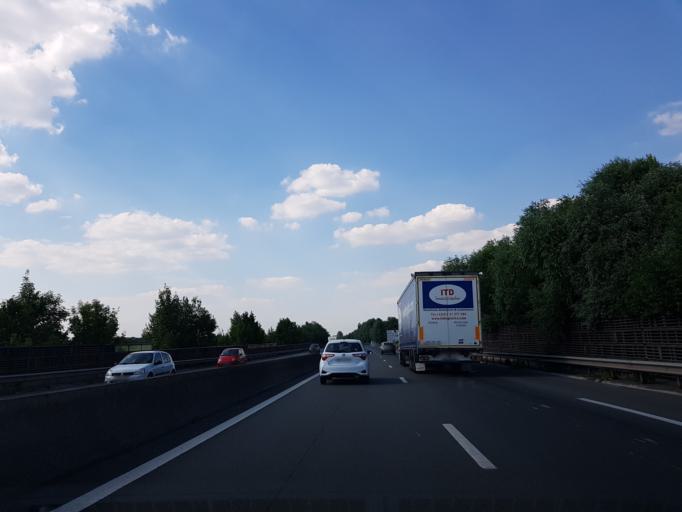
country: FR
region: Nord-Pas-de-Calais
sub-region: Departement du Nord
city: Bruille-lez-Marchiennes
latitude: 50.3594
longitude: 3.2622
